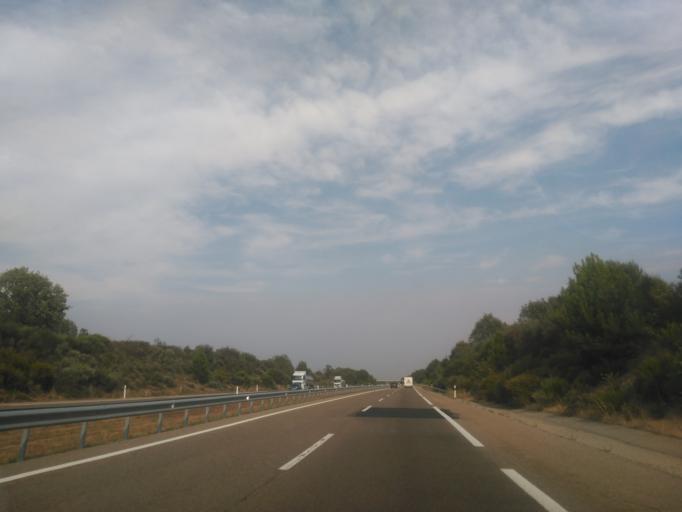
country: ES
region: Castille and Leon
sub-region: Provincia de Zamora
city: Asturianos
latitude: 42.0451
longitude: -6.4942
